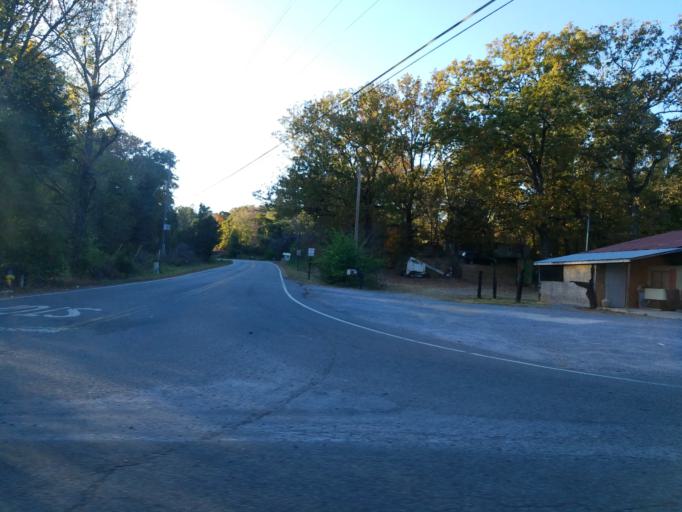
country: US
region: Georgia
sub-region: Bartow County
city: Adairsville
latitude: 34.3001
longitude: -84.9394
